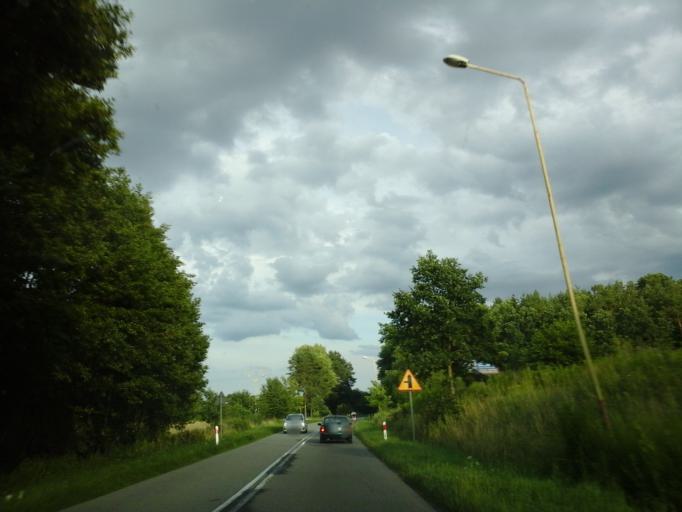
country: PL
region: West Pomeranian Voivodeship
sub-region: Powiat kamienski
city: Golczewo
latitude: 53.8176
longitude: 14.9928
